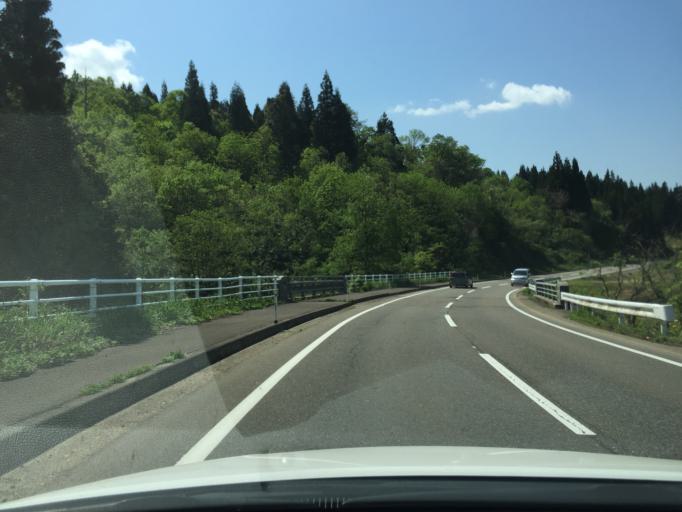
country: JP
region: Niigata
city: Kamo
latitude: 37.5900
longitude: 139.0948
